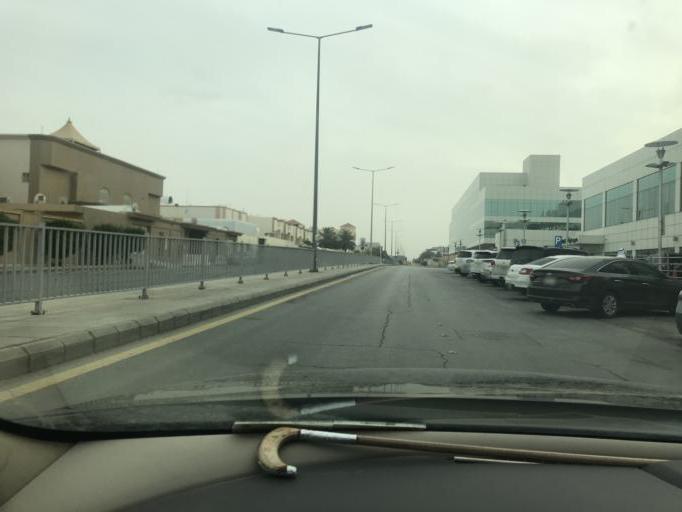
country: SA
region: Ar Riyad
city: Riyadh
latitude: 24.7205
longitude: 46.7758
